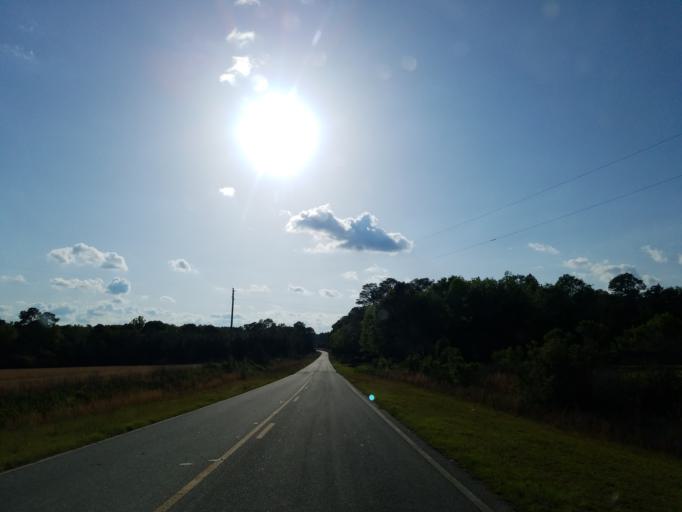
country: US
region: Georgia
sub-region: Turner County
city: Ashburn
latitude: 31.6090
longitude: -83.5682
